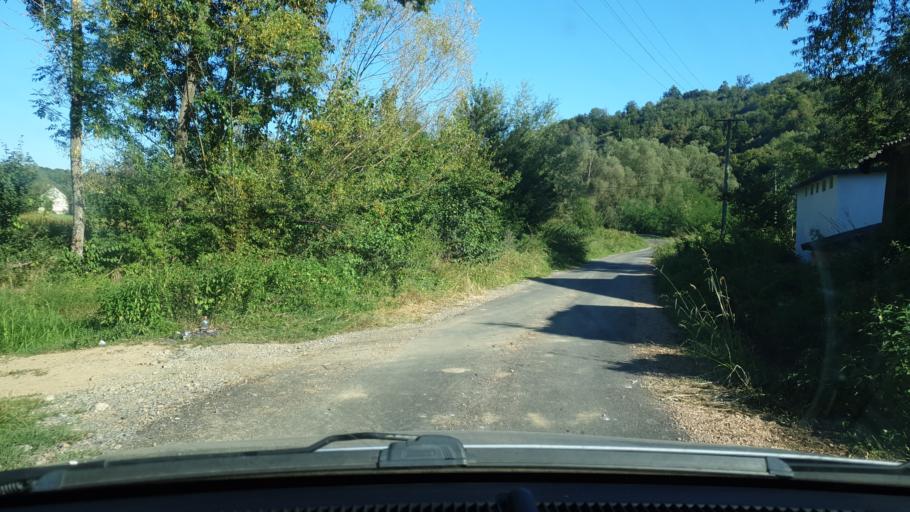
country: RS
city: Jarebice
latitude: 44.5013
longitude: 19.4901
